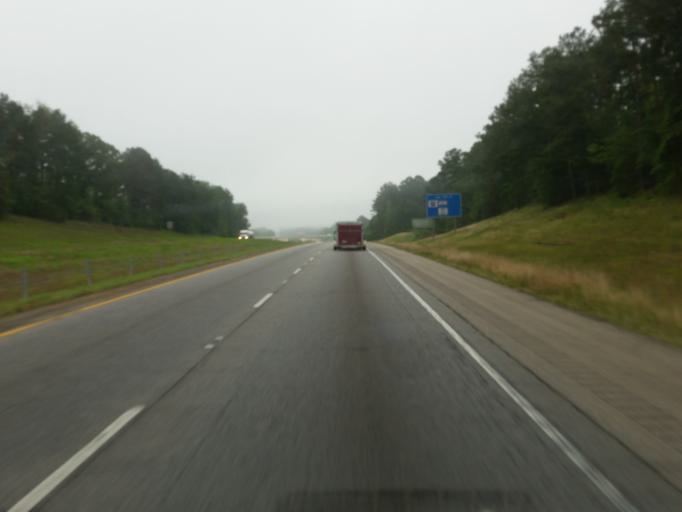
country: US
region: Louisiana
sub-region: Webster Parish
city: Minden
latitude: 32.5919
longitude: -93.3034
